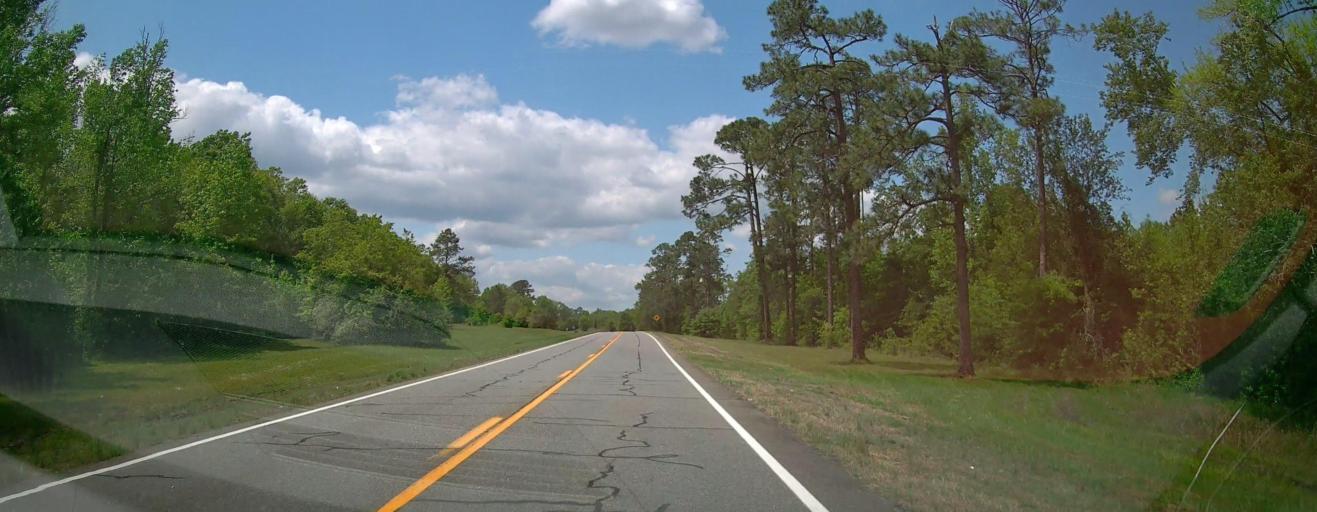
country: US
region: Georgia
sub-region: Treutlen County
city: Soperton
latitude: 32.4289
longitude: -82.6666
